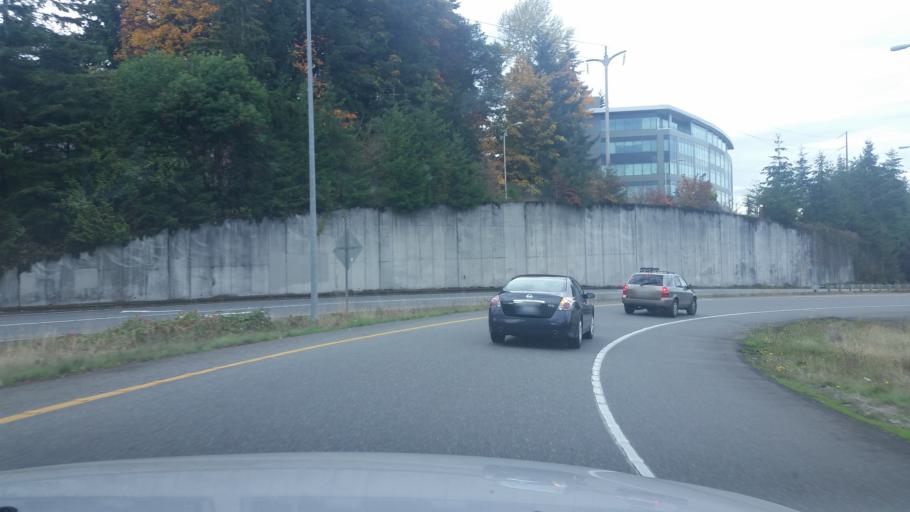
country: US
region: Washington
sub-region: King County
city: Eastgate
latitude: 47.5775
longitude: -122.1411
